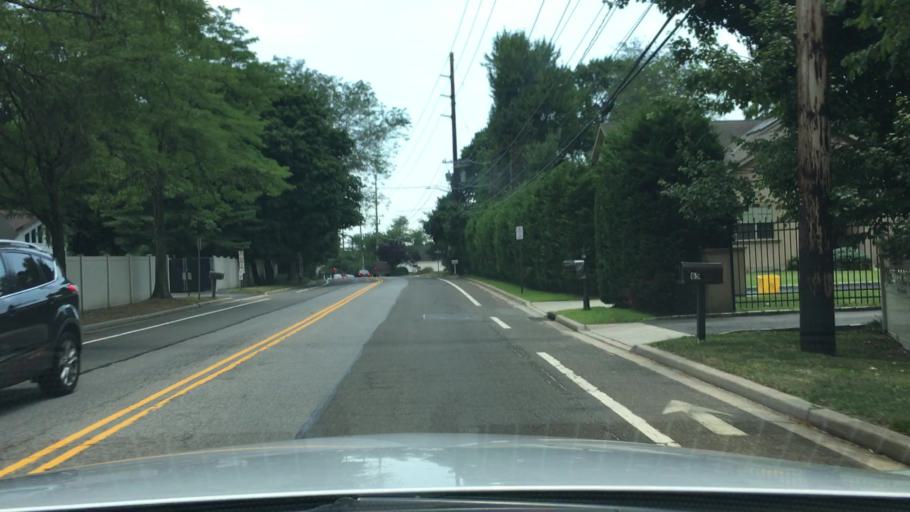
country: US
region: New York
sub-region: Nassau County
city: Woodbury
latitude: 40.8109
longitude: -73.4767
